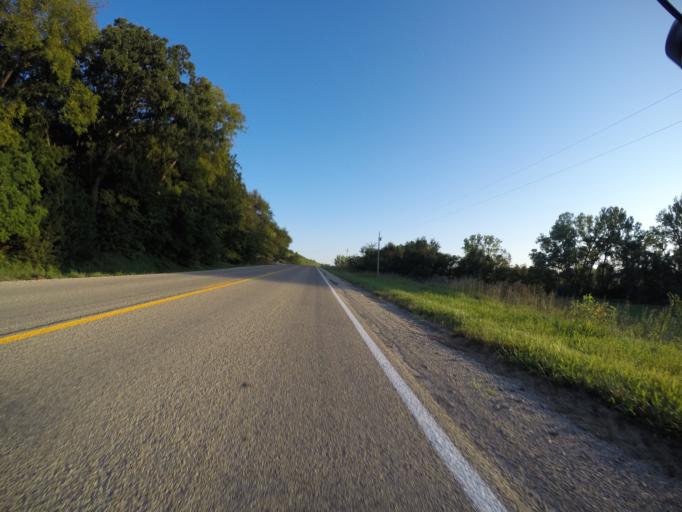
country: US
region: Kansas
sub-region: Riley County
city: Manhattan
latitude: 39.1480
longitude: -96.5580
